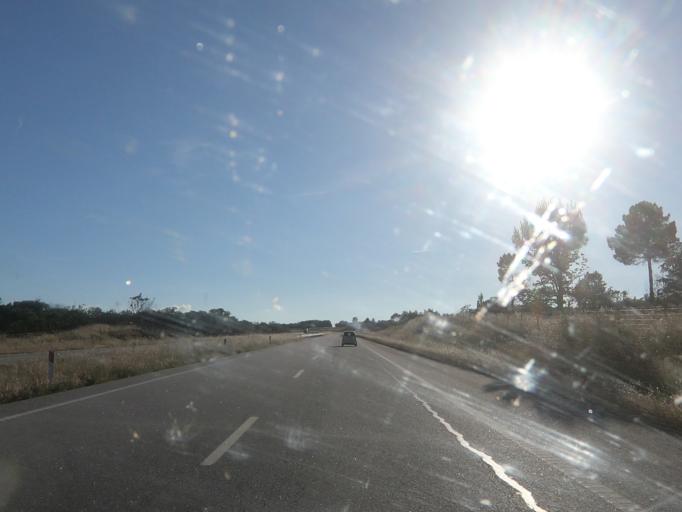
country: PT
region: Guarda
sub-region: Guarda
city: Sequeira
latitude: 40.6010
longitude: -7.1183
